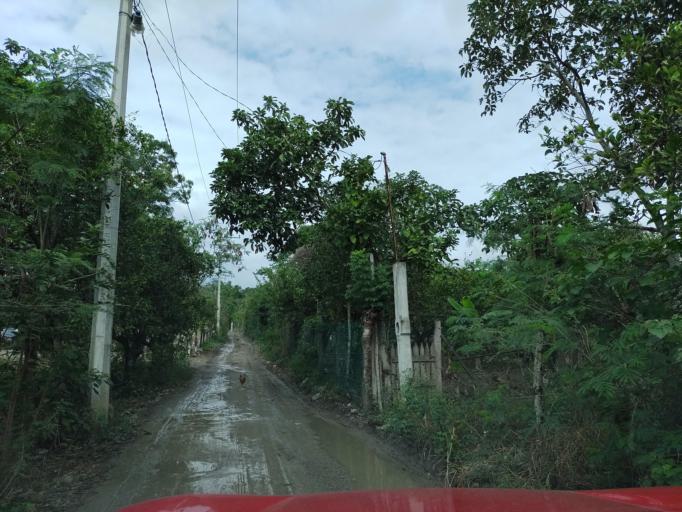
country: MX
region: Veracruz
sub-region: Papantla
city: El Chote
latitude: 20.4359
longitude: -97.3768
